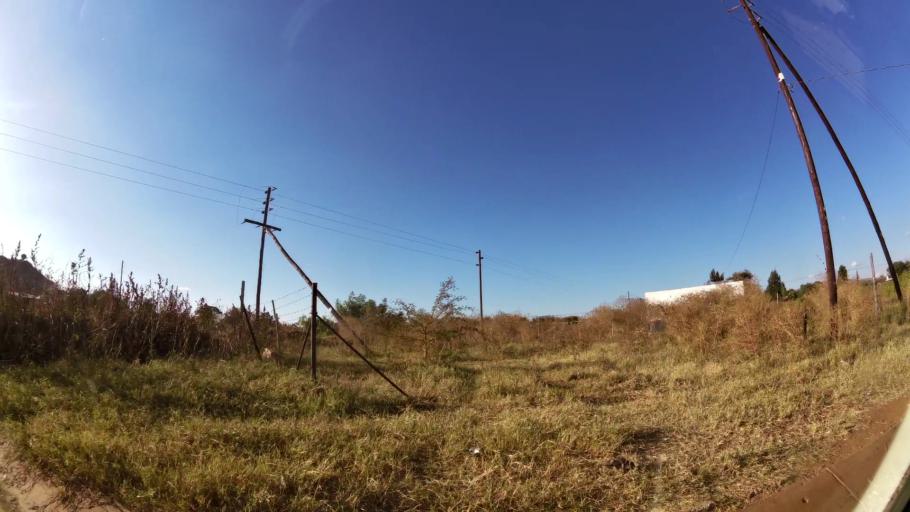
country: ZA
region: Limpopo
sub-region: Waterberg District Municipality
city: Mokopane
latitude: -24.1614
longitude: 28.9803
